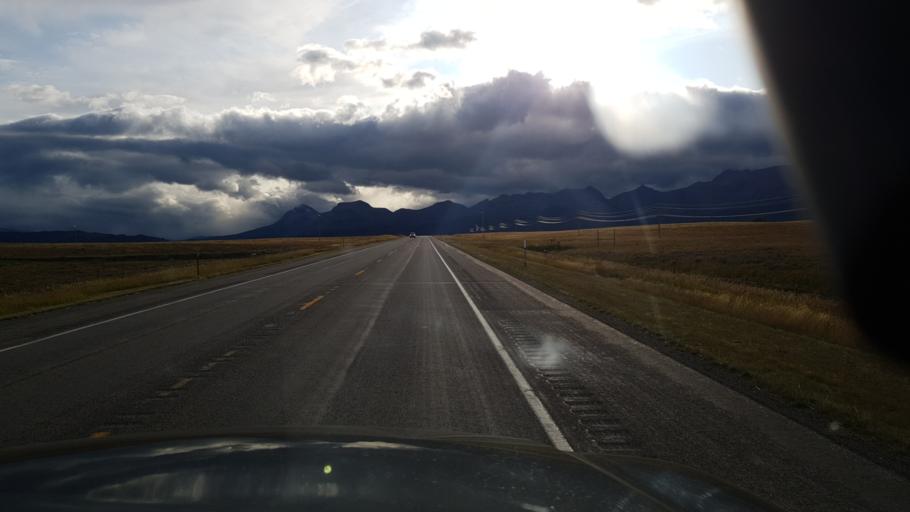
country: US
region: Montana
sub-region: Glacier County
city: South Browning
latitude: 48.4651
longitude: -113.1600
